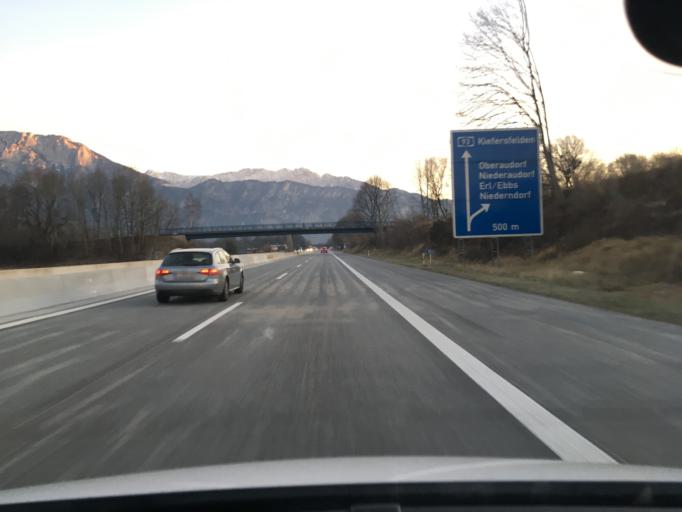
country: DE
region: Bavaria
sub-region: Upper Bavaria
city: Oberaudorf
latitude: 47.6529
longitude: 12.1862
